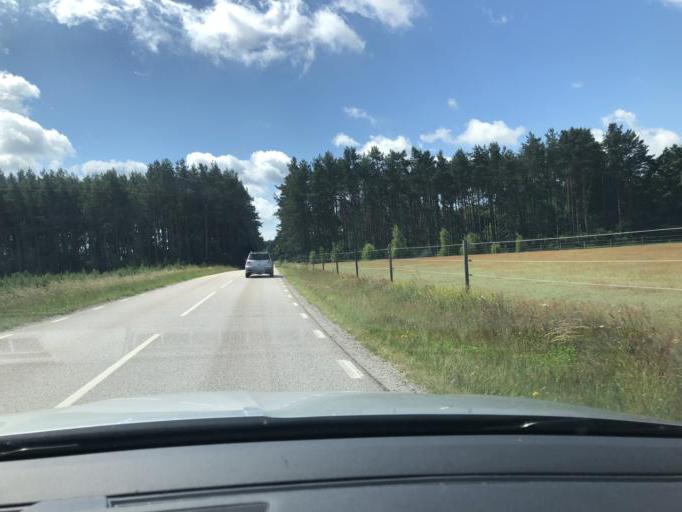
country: SE
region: Blekinge
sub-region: Solvesborgs Kommun
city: Soelvesborg
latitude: 56.0799
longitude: 14.6083
